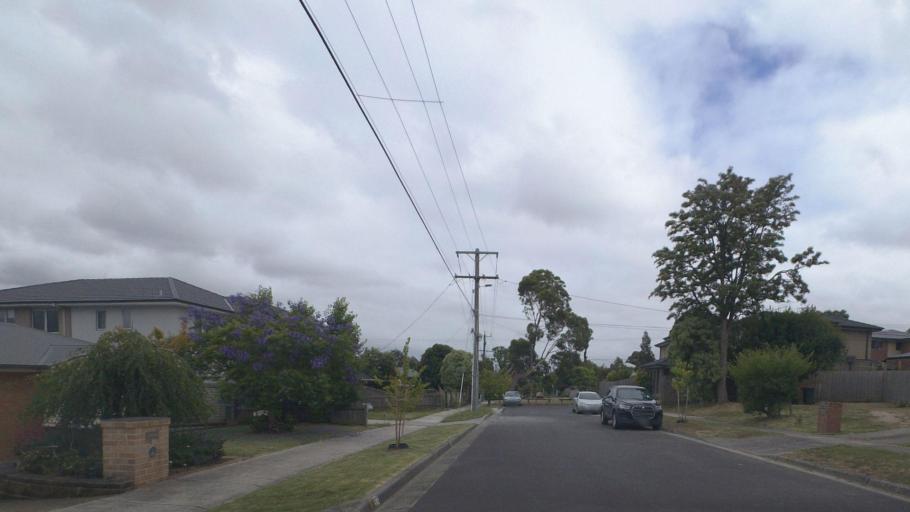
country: AU
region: Victoria
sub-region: Knox
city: Boronia
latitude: -37.8726
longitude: 145.2661
